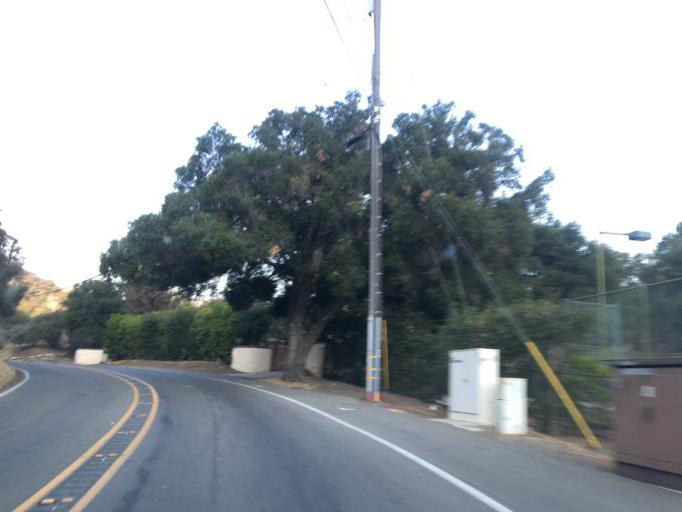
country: US
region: California
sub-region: Los Angeles County
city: Malibu Beach
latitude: 34.0796
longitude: -118.6900
